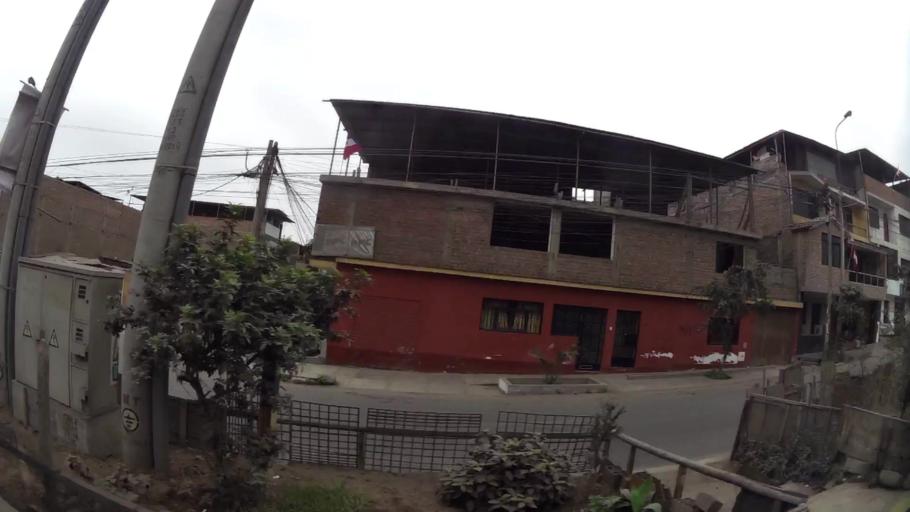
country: PE
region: Lima
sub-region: Lima
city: Surco
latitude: -12.1448
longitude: -76.9689
